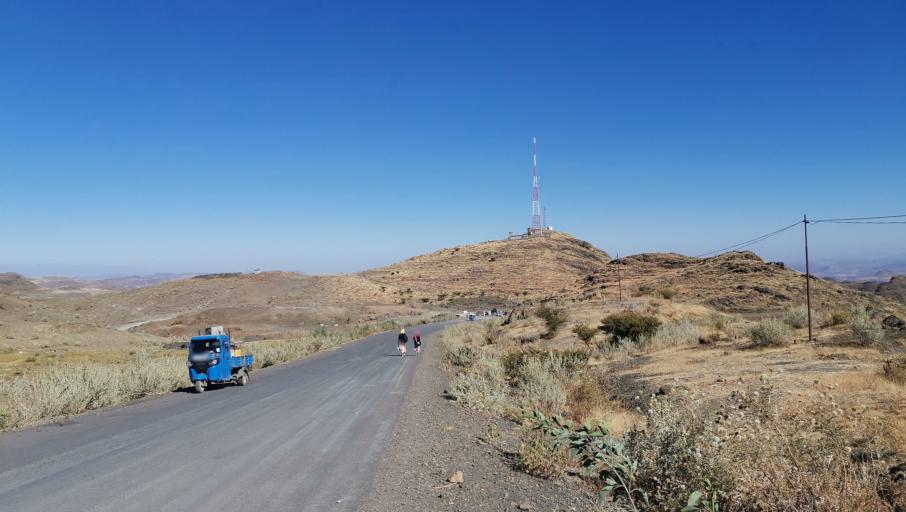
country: ET
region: Tigray
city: Korem
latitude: 12.6180
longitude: 39.0442
